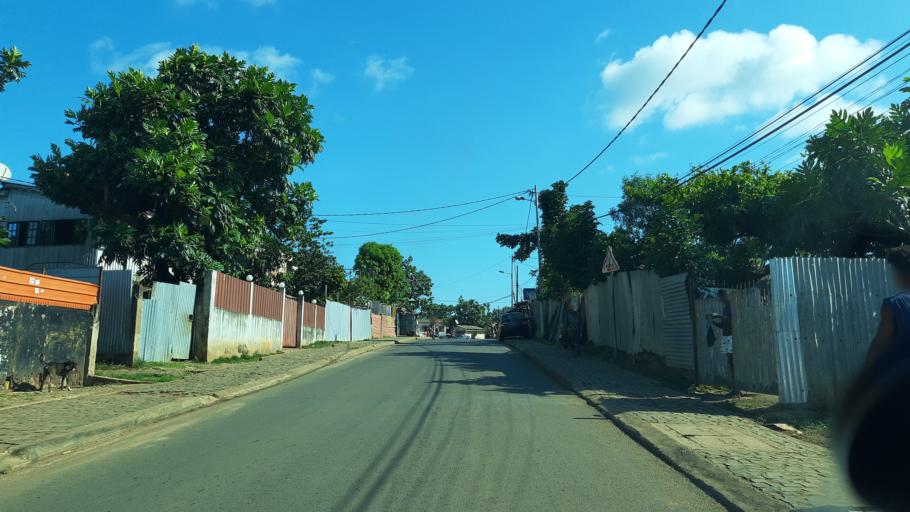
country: ST
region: Sao Tome Island
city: Sao Tome
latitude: 0.3238
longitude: 6.7281
